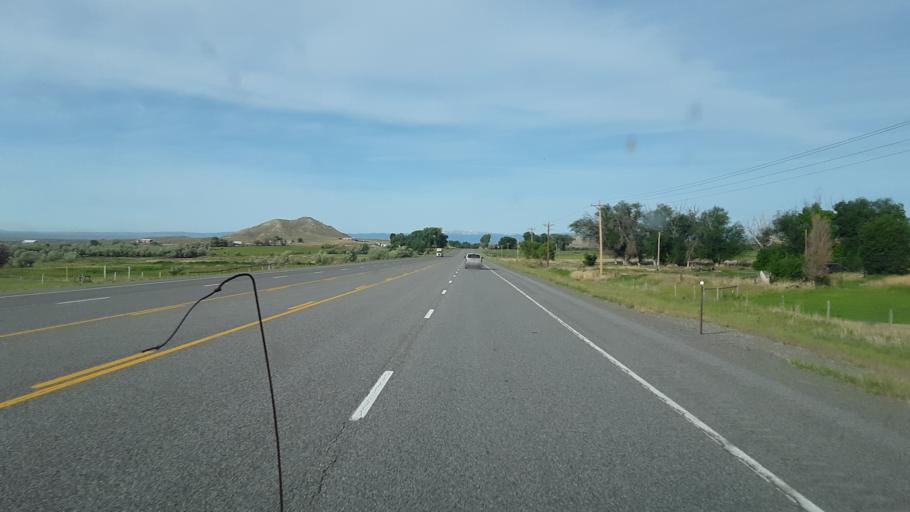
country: US
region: Wyoming
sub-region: Fremont County
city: Riverton
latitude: 43.1351
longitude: -108.3000
